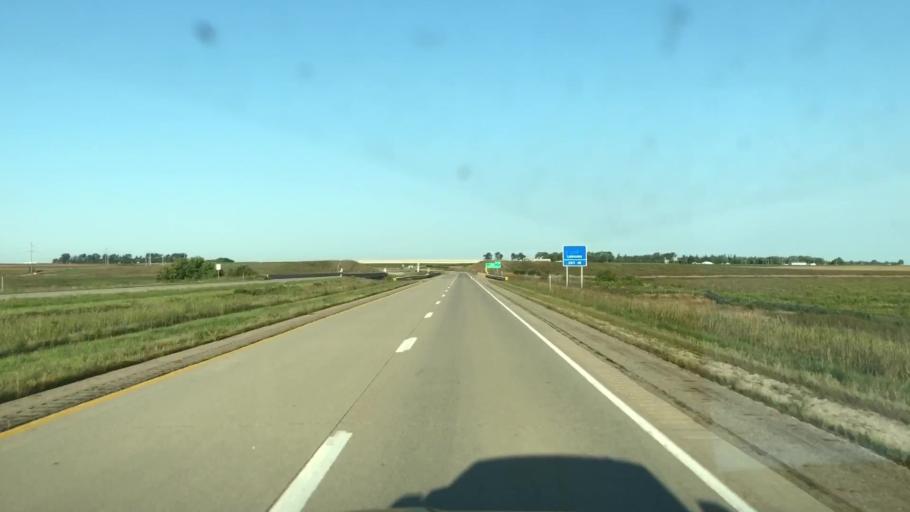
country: US
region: Iowa
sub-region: Osceola County
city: Sibley
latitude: 43.3845
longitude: -95.7347
